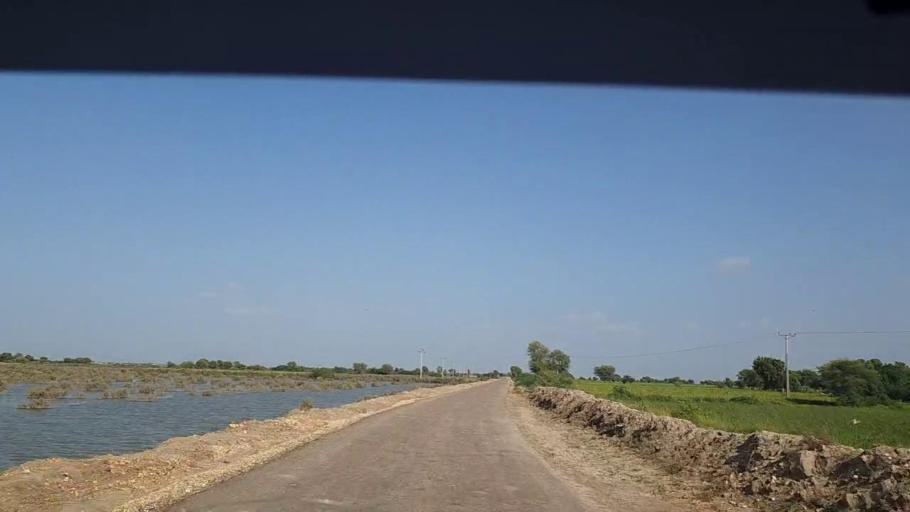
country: PK
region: Sindh
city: Kadhan
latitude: 24.4652
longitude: 68.8383
